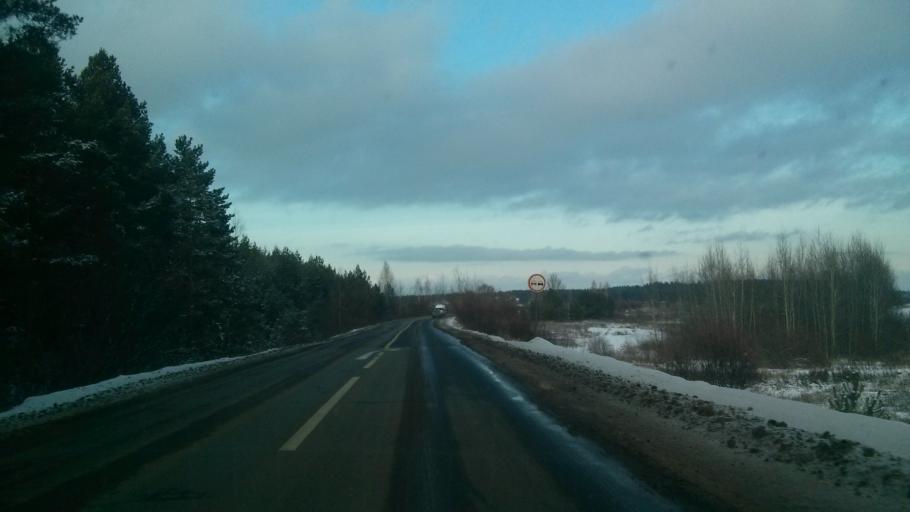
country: RU
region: Nizjnij Novgorod
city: Navashino
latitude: 55.5905
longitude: 42.1516
